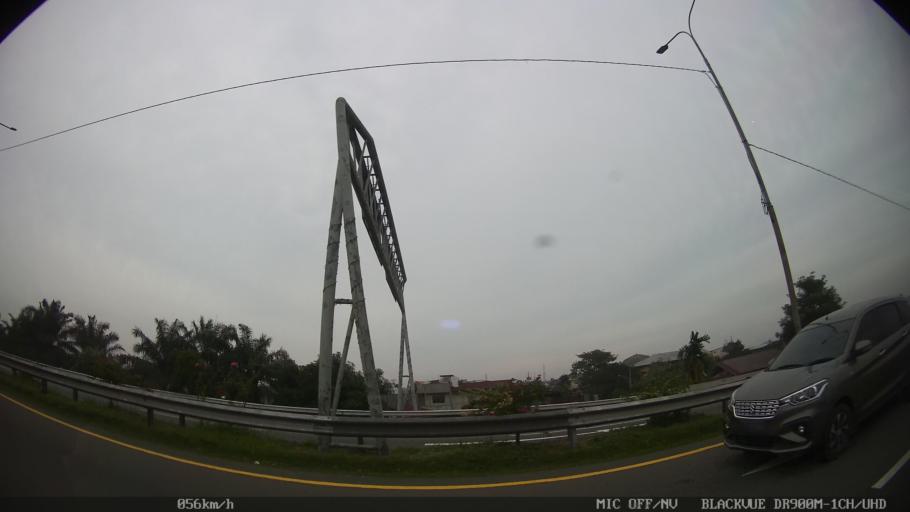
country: ID
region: North Sumatra
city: Medan
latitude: 3.5940
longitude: 98.7241
